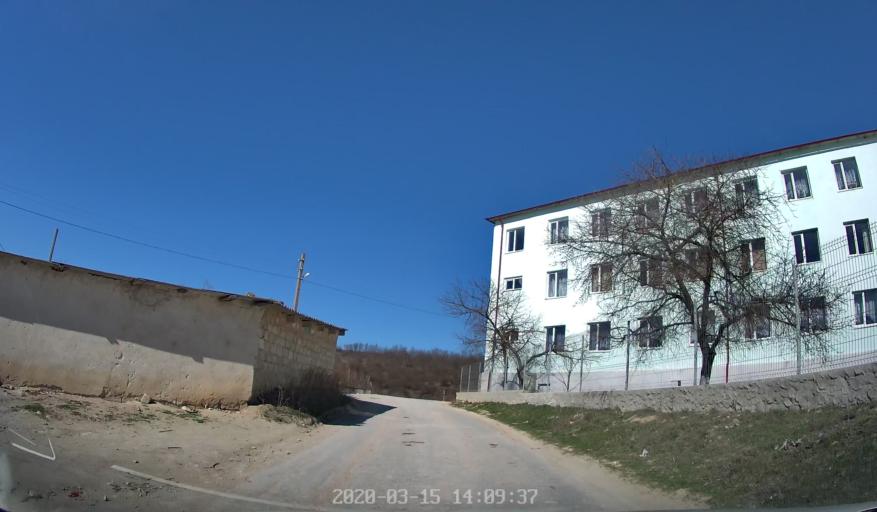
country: MD
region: Orhei
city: Orhei
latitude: 47.3113
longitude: 28.9320
